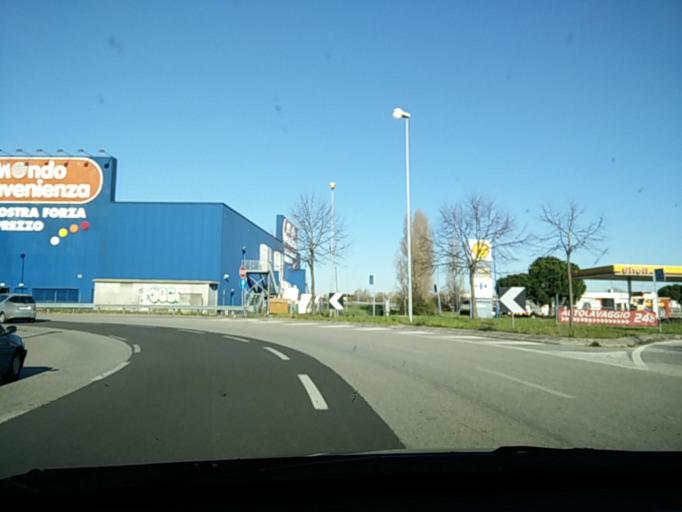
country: IT
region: Veneto
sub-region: Provincia di Venezia
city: Dese
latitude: 45.5475
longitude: 12.3053
